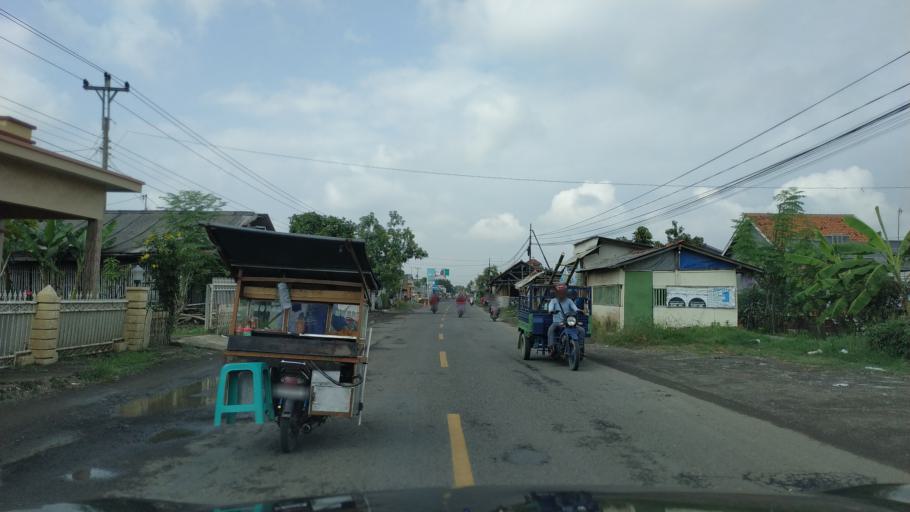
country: ID
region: Central Java
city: Ketanggungan
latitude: -6.8856
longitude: 108.8855
